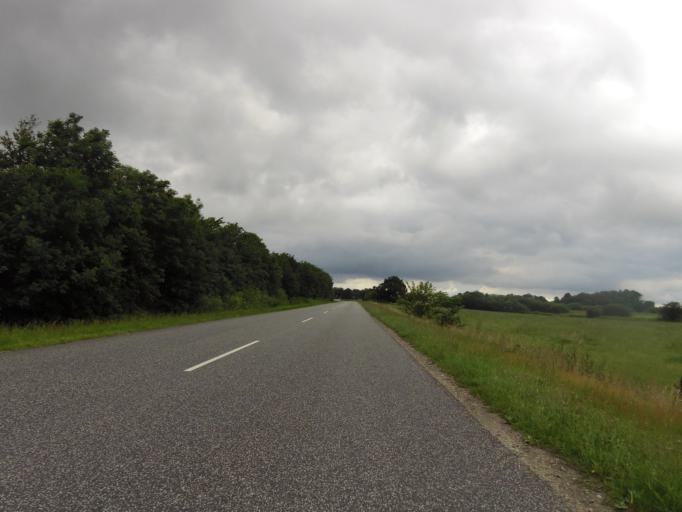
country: DK
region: South Denmark
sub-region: Tonder Kommune
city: Toftlund
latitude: 55.1196
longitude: 9.0740
